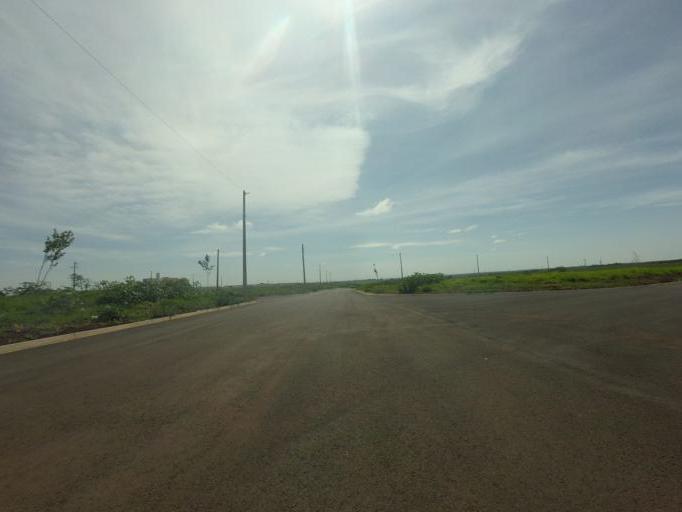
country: BR
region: Sao Paulo
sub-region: Piracicaba
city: Piracicaba
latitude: -22.7647
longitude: -47.5865
